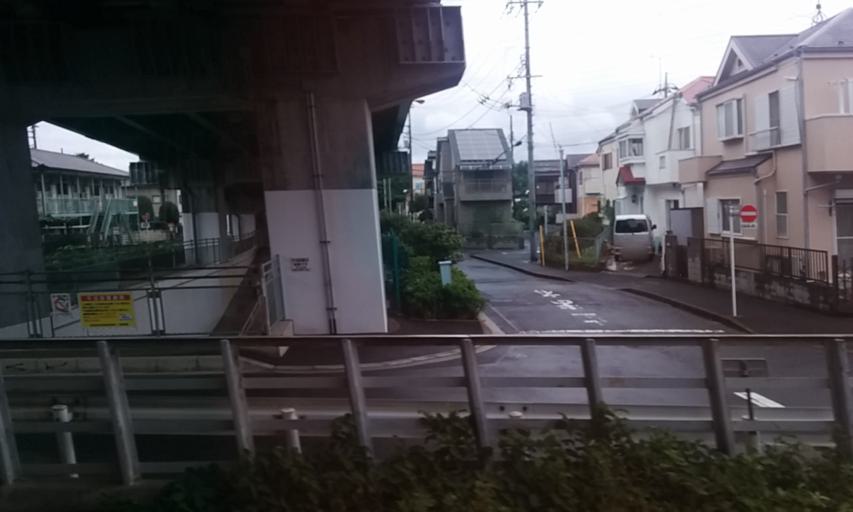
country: JP
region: Tokyo
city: Hino
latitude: 35.6497
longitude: 139.3831
